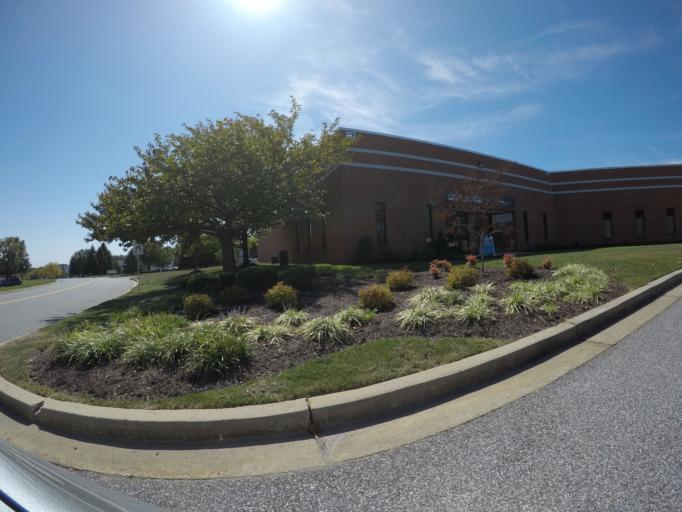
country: US
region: Maryland
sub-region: Harford County
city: Edgewood
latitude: 39.4486
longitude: -76.2976
